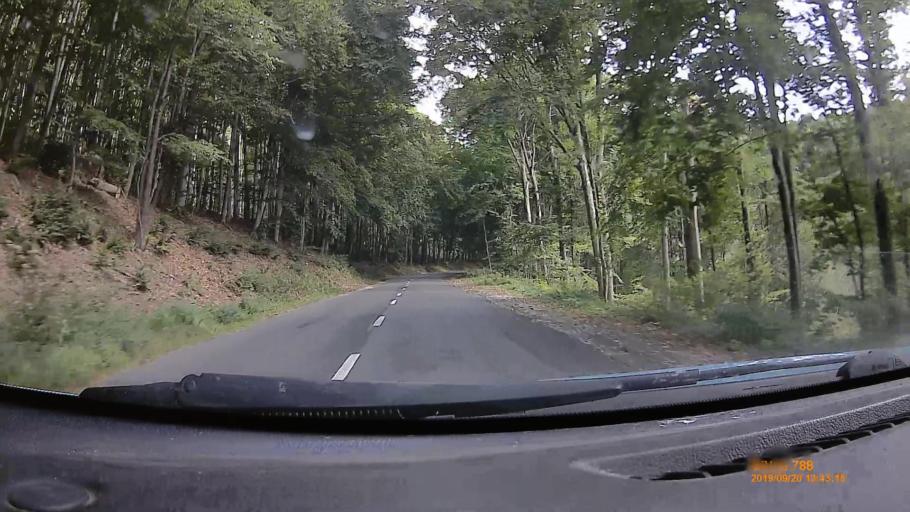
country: HU
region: Heves
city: Szilvasvarad
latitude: 48.0590
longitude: 20.5518
